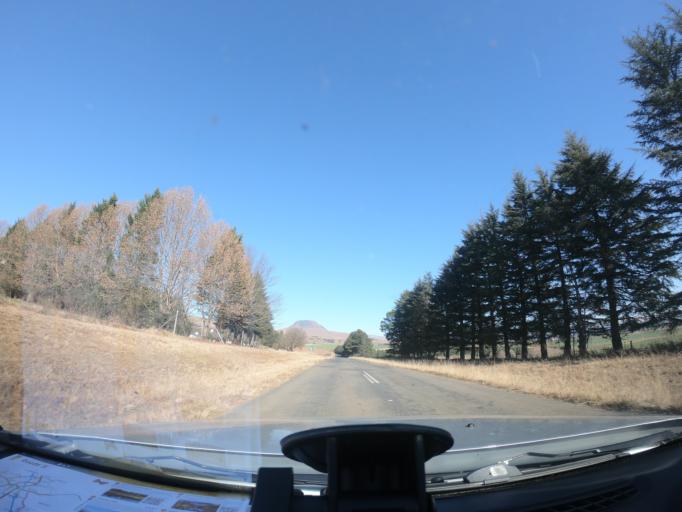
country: ZA
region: KwaZulu-Natal
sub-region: uMgungundlovu District Municipality
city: Mooirivier
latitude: -29.3285
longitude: 29.8245
